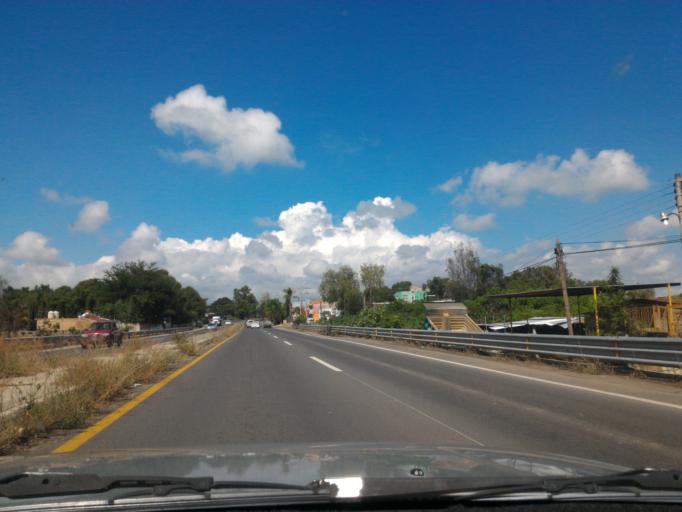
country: MX
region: Jalisco
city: Arenal
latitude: 20.7473
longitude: -103.6439
